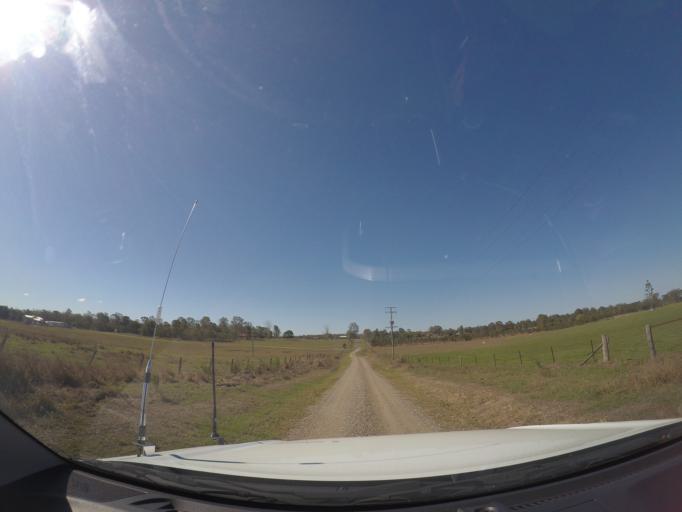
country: AU
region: Queensland
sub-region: Logan
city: North Maclean
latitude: -27.7693
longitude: 153.0467
